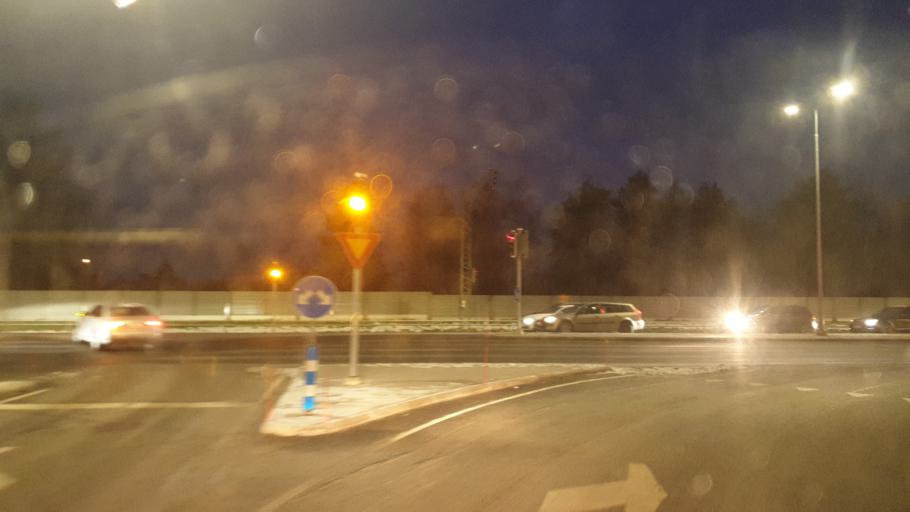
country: FI
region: Southern Savonia
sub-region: Savonlinna
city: Savonlinna
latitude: 61.8775
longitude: 28.8234
